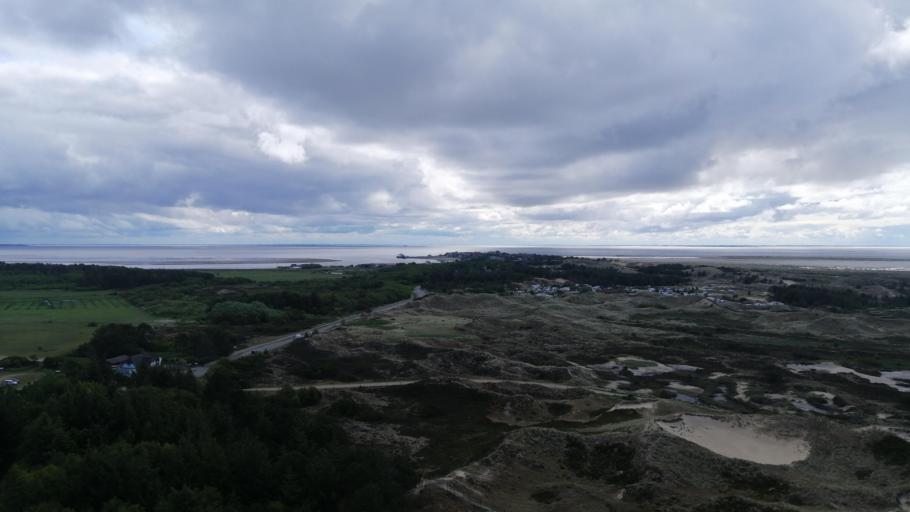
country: DE
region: Schleswig-Holstein
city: Nebel
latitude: 54.6311
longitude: 8.3549
